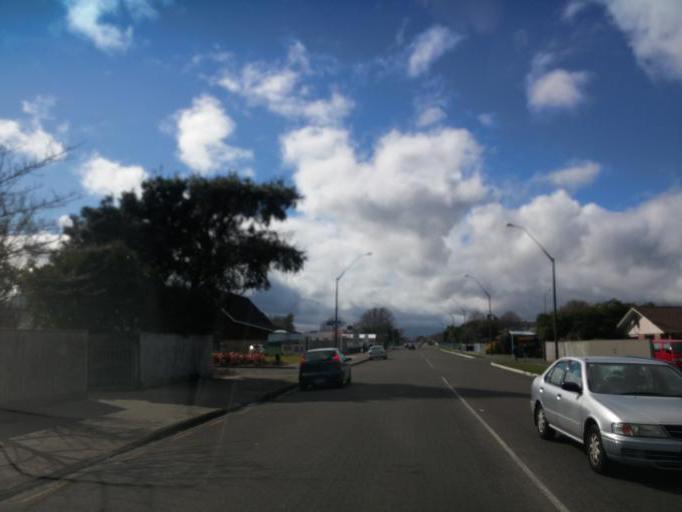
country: NZ
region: Manawatu-Wanganui
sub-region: Palmerston North City
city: Palmerston North
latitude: -40.3623
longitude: 175.6071
